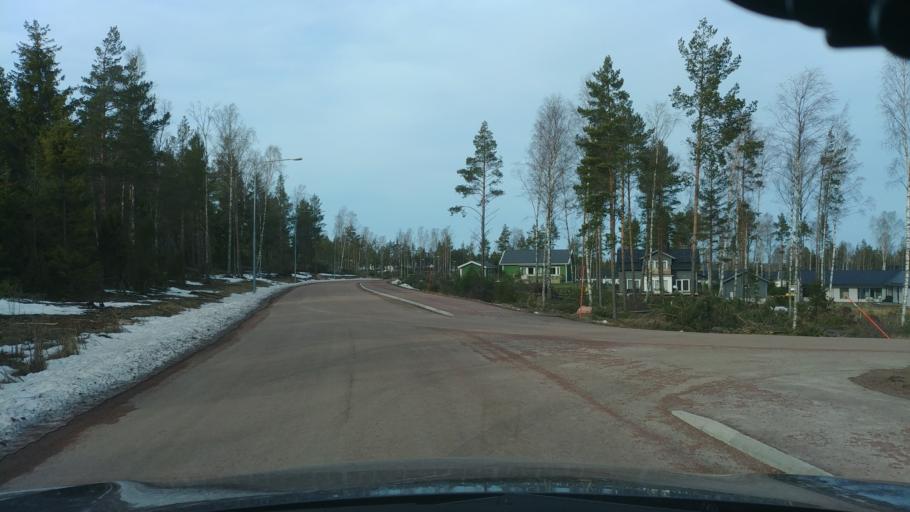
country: AX
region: Mariehamns stad
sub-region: Mariehamn
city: Mariehamn
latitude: 60.1004
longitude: 19.8939
